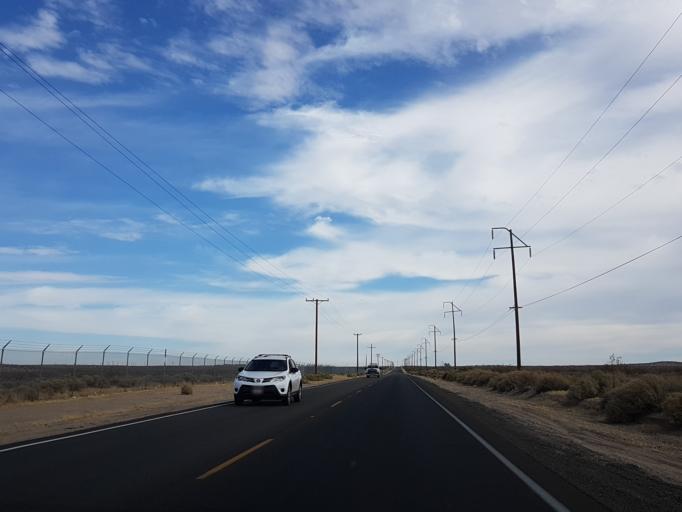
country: US
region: California
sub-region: Kern County
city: Ridgecrest
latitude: 35.6226
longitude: -117.6211
